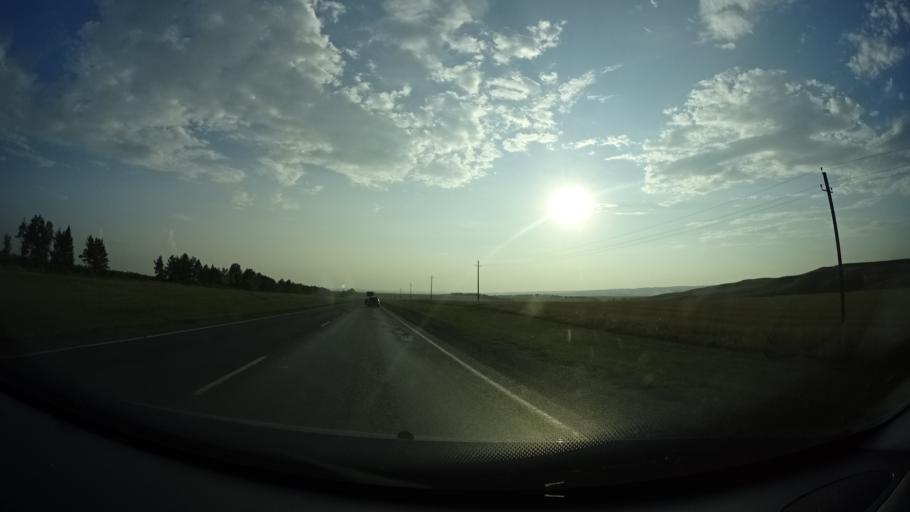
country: RU
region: Samara
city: Kamyshla
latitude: 54.0617
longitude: 52.1131
